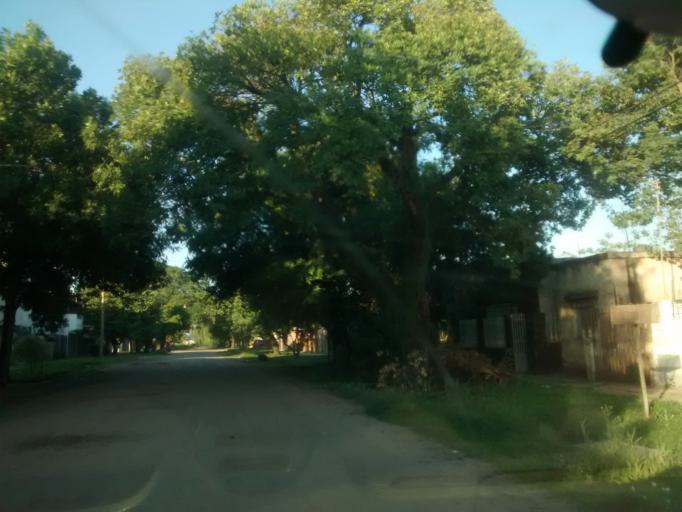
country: AR
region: Chaco
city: Resistencia
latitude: -27.4673
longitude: -58.9737
